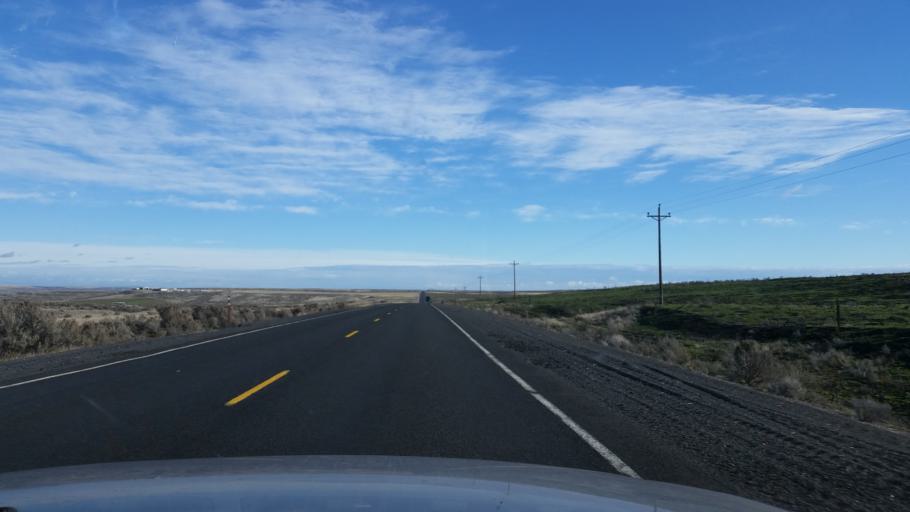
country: US
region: Washington
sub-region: Grant County
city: Warden
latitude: 47.3172
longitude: -118.8357
